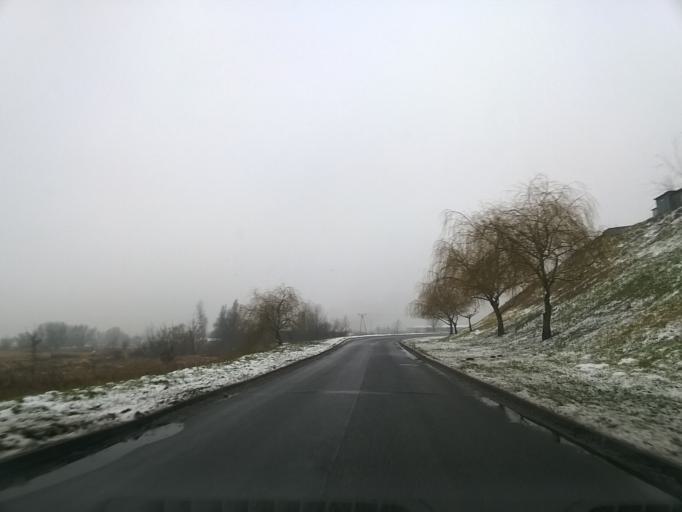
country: PL
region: Kujawsko-Pomorskie
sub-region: Powiat swiecki
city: Swiecie
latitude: 53.4014
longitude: 18.4252
